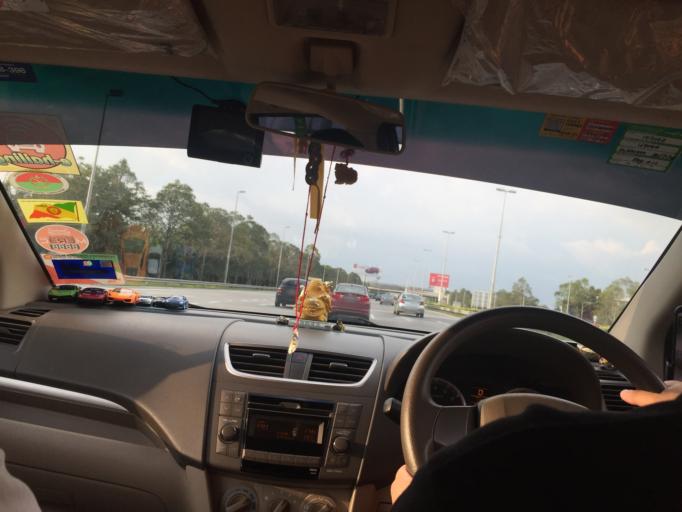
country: MY
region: Negeri Sembilan
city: Kampung Baharu Nilai
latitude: 2.7840
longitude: 101.6737
